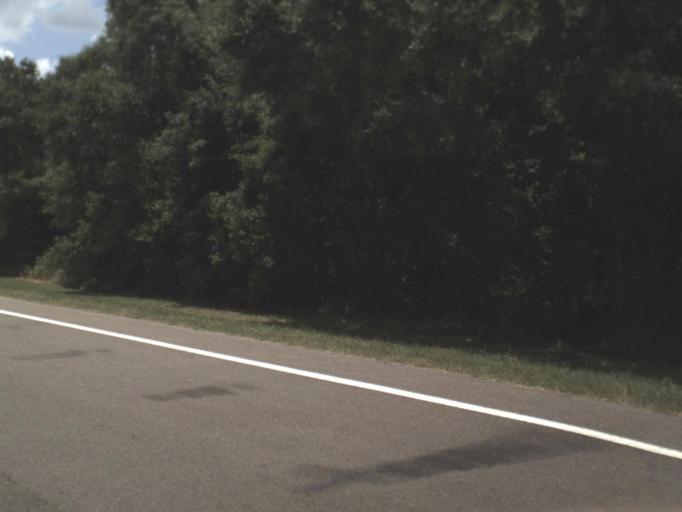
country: US
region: Florida
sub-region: Alachua County
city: Alachua
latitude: 29.8847
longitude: -82.4232
